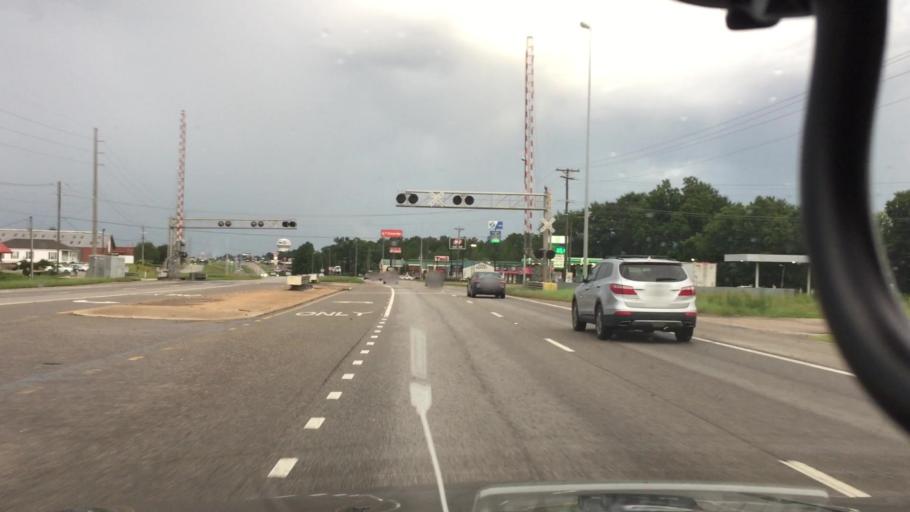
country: US
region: Alabama
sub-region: Pike County
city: Troy
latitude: 31.7915
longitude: -85.9764
